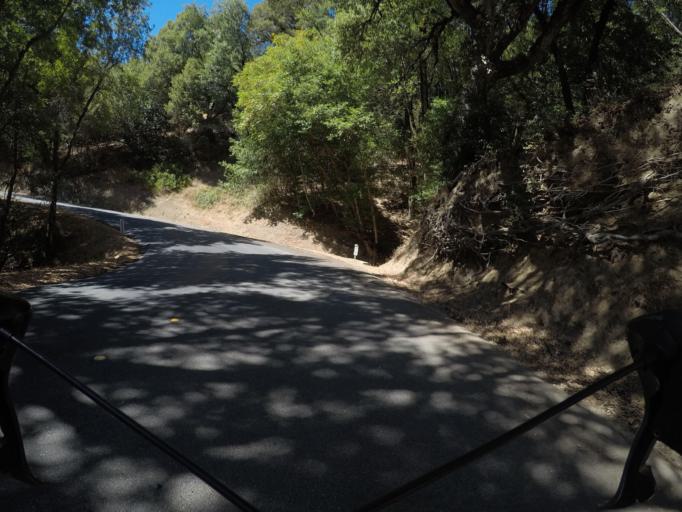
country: US
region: California
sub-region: San Mateo County
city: Portola Valley
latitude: 37.3168
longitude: -122.1954
